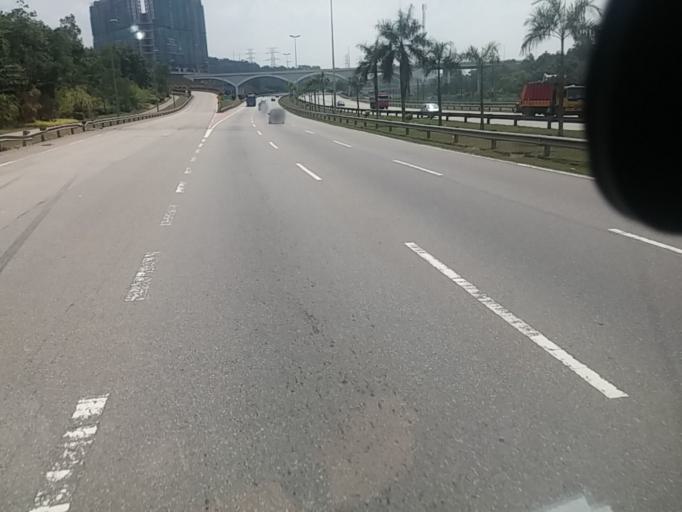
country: MY
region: Putrajaya
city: Putrajaya
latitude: 2.9551
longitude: 101.6580
